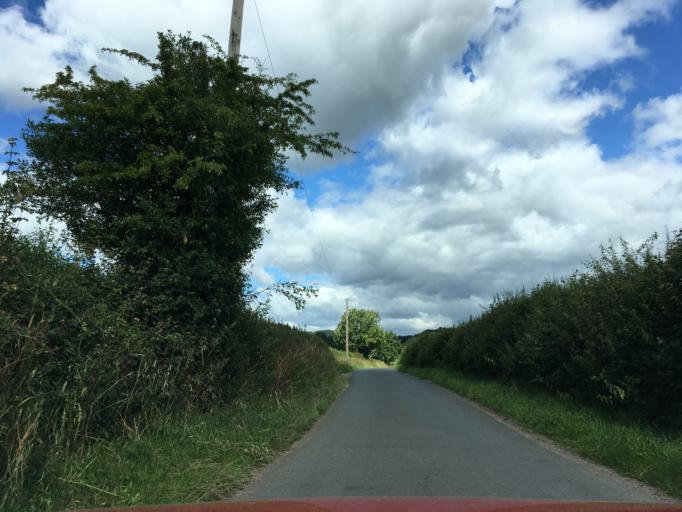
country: GB
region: England
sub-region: Gloucestershire
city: Mitcheldean
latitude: 51.8405
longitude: -2.4312
